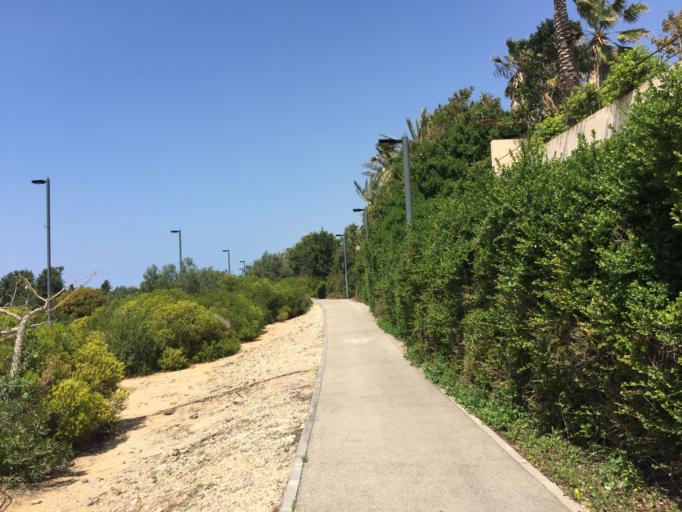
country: IL
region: Haifa
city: Qesarya
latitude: 32.4926
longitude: 34.9041
